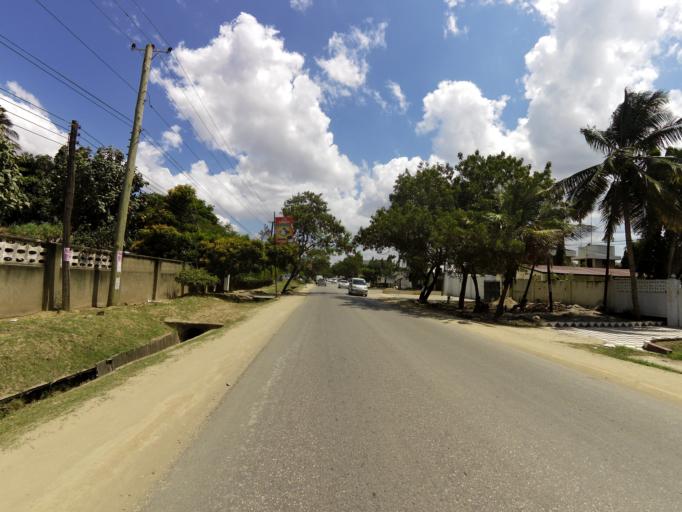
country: TZ
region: Dar es Salaam
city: Magomeni
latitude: -6.7645
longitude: 39.2491
